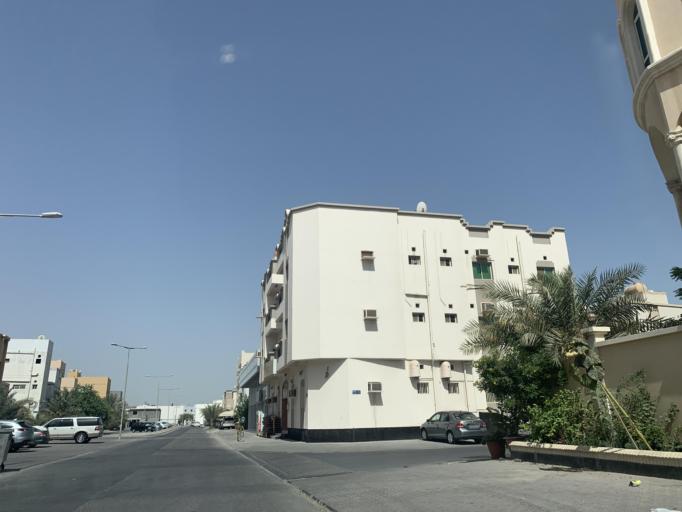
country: BH
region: Northern
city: Sitrah
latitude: 26.1591
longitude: 50.6100
